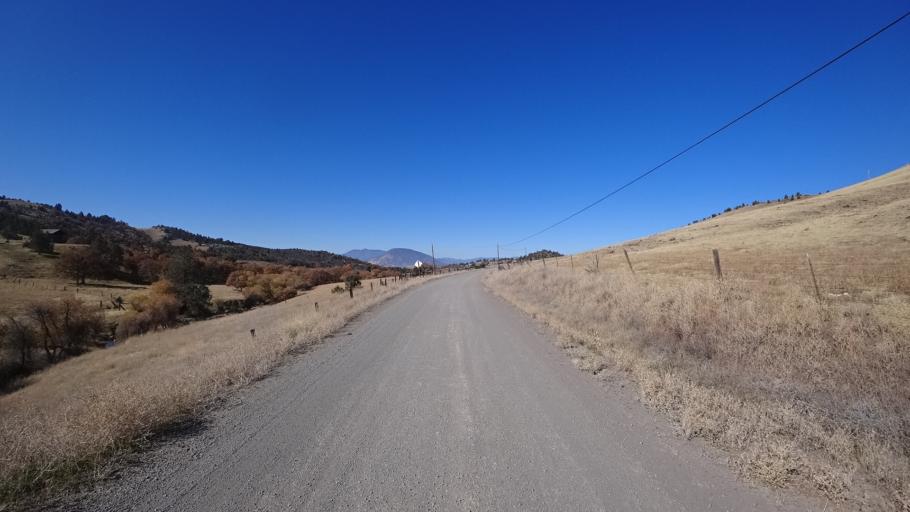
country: US
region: California
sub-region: Siskiyou County
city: Montague
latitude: 41.7952
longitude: -122.3643
